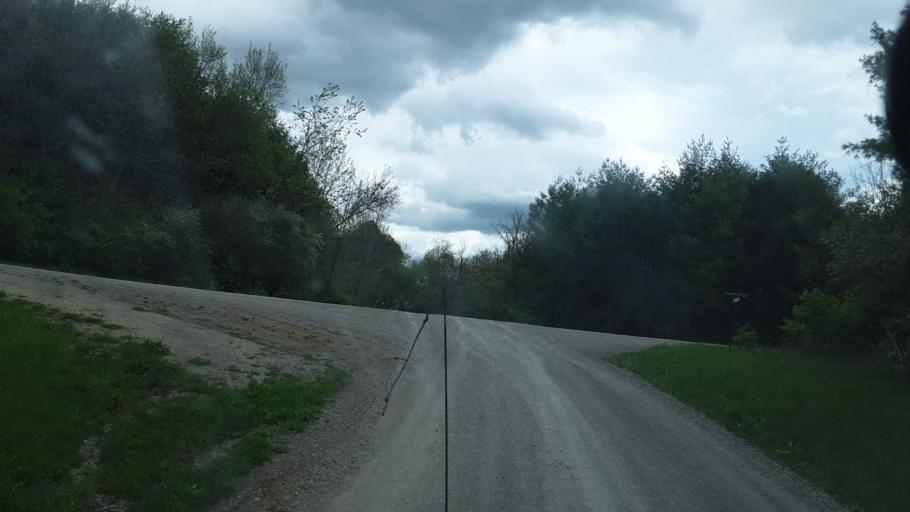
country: US
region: Ohio
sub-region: Noble County
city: Caldwell
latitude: 39.7728
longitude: -81.6173
